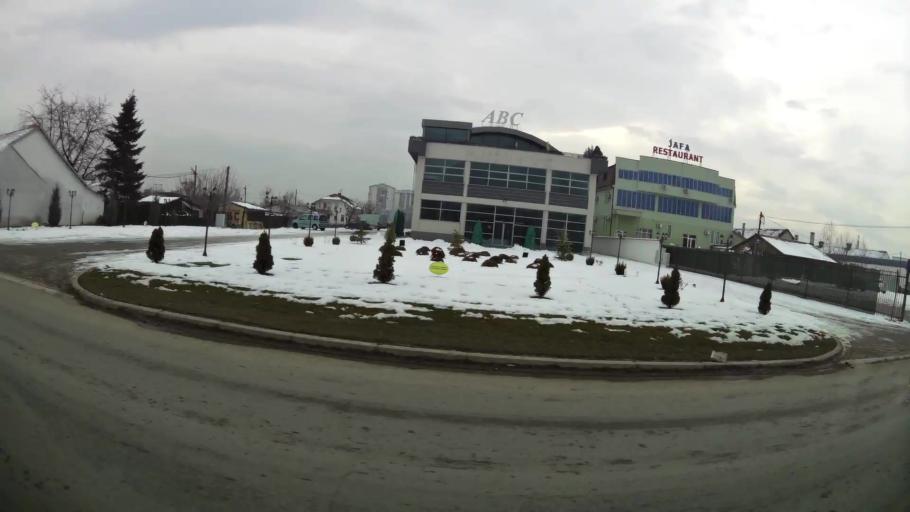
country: MK
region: Butel
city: Butel
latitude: 42.0281
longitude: 21.4410
